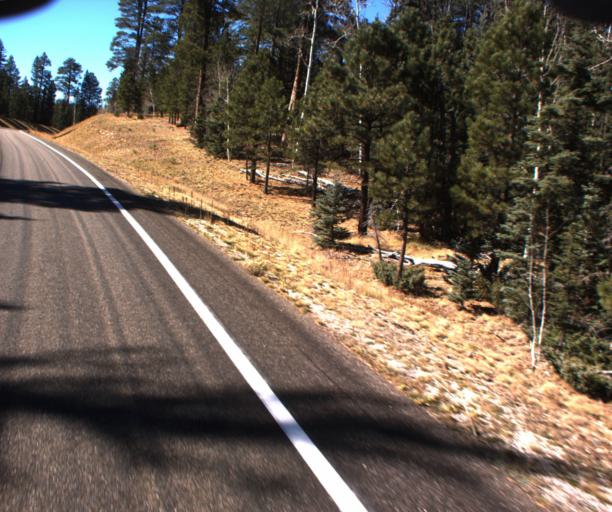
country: US
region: Arizona
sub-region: Coconino County
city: Grand Canyon
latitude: 36.5349
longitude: -112.1543
